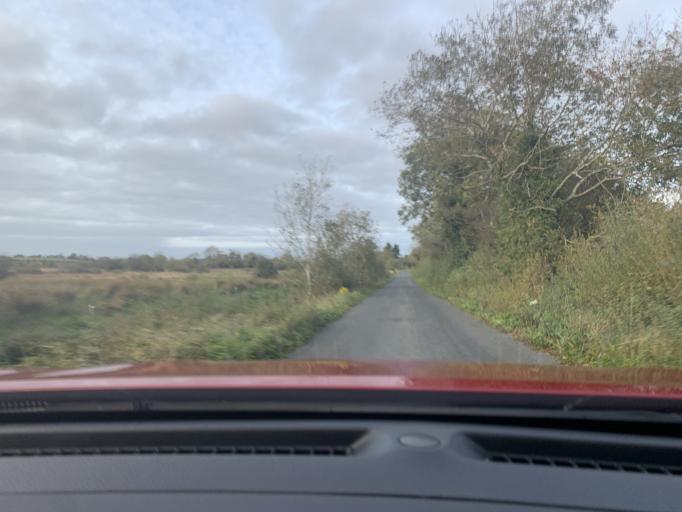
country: IE
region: Connaught
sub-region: Roscommon
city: Ballaghaderreen
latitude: 53.9960
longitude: -8.6080
